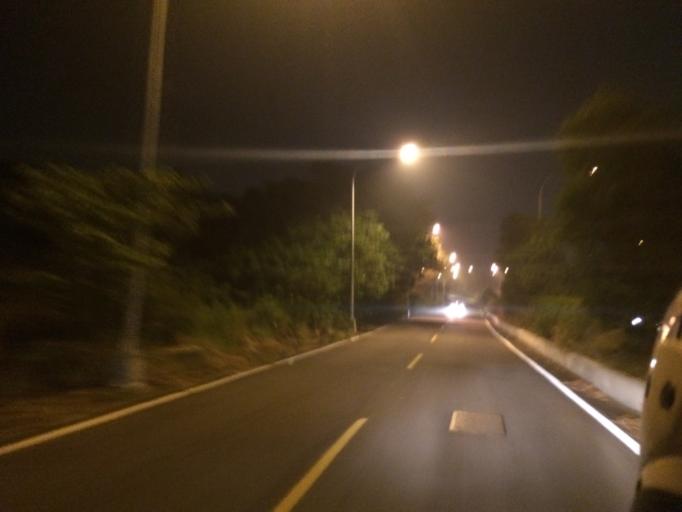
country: TW
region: Taiwan
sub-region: Hsinchu
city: Hsinchu
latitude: 24.7318
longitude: 120.9049
